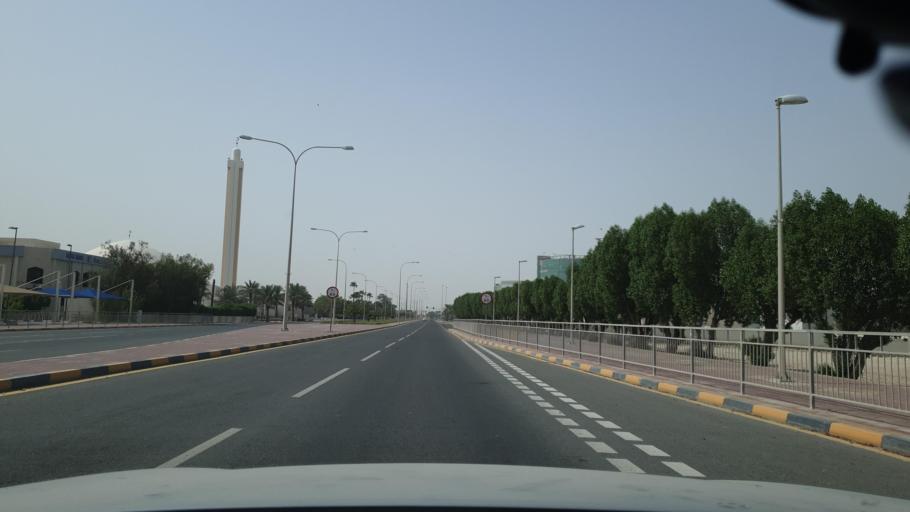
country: QA
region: Al Wakrah
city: Umm Sa'id
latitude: 24.9914
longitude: 51.5491
